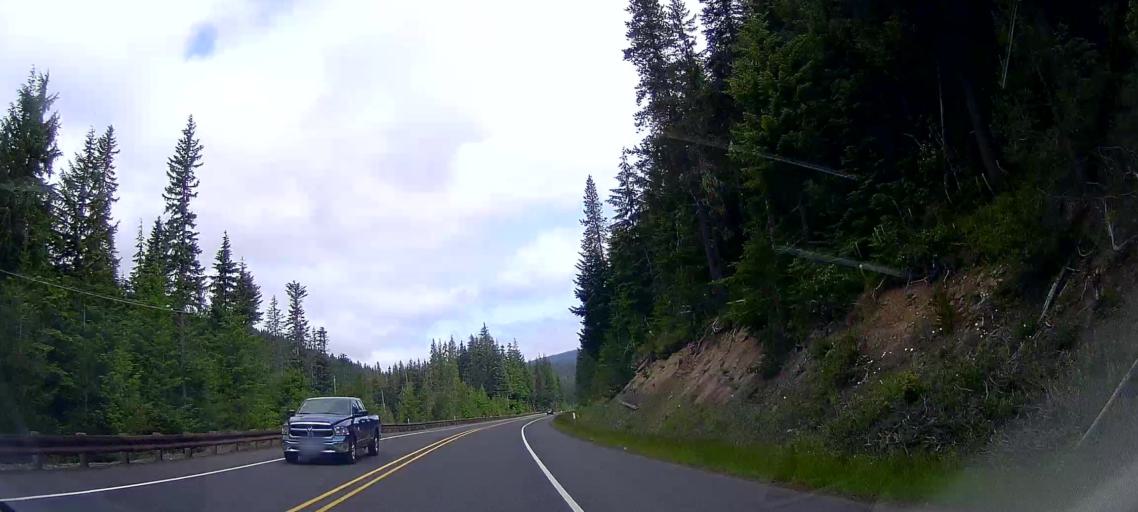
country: US
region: Oregon
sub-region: Clackamas County
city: Mount Hood Village
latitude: 45.2673
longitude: -121.7177
